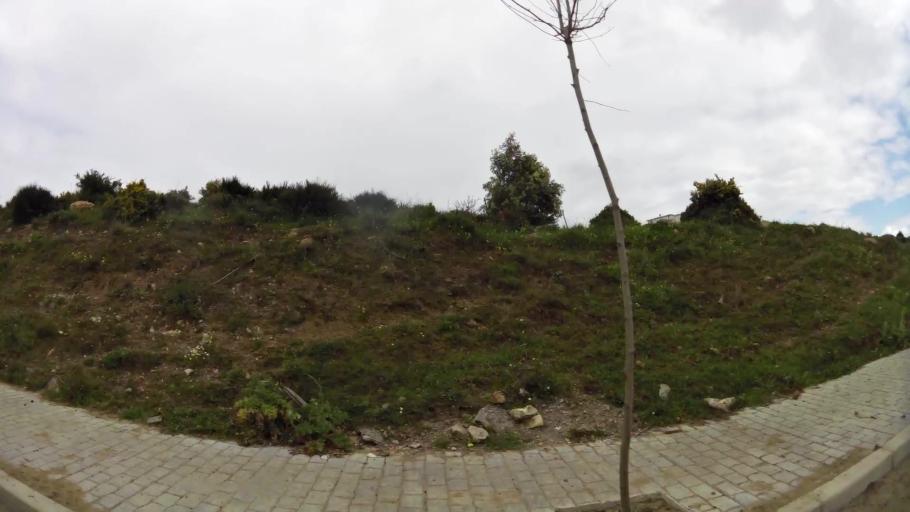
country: MA
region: Tanger-Tetouan
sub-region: Tanger-Assilah
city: Boukhalef
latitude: 35.7778
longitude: -5.8640
